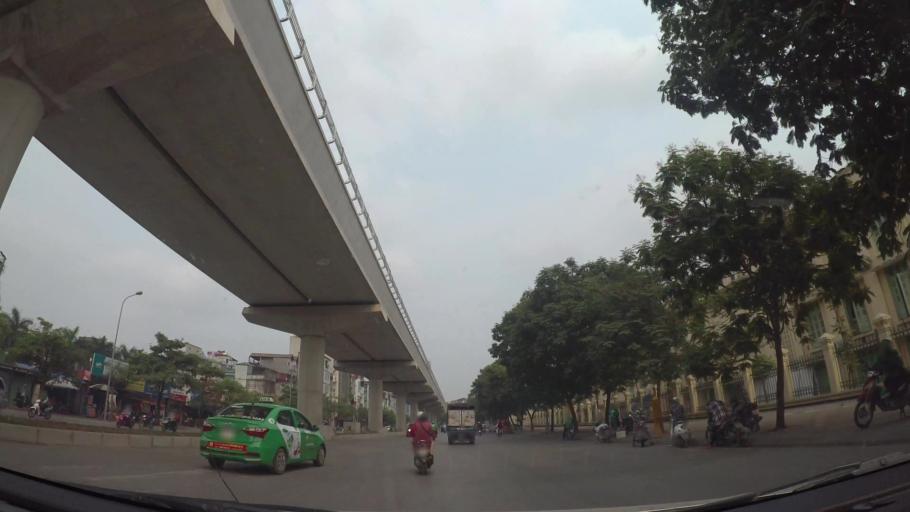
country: VN
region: Ha Noi
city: Cau Dien
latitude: 21.0372
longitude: 105.7752
